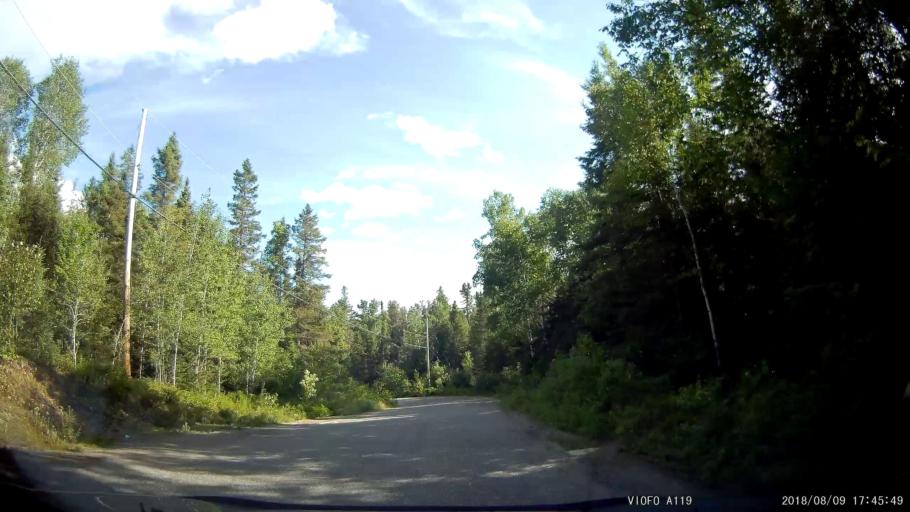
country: CA
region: Ontario
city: Rayside-Balfour
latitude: 46.5978
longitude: -81.5339
